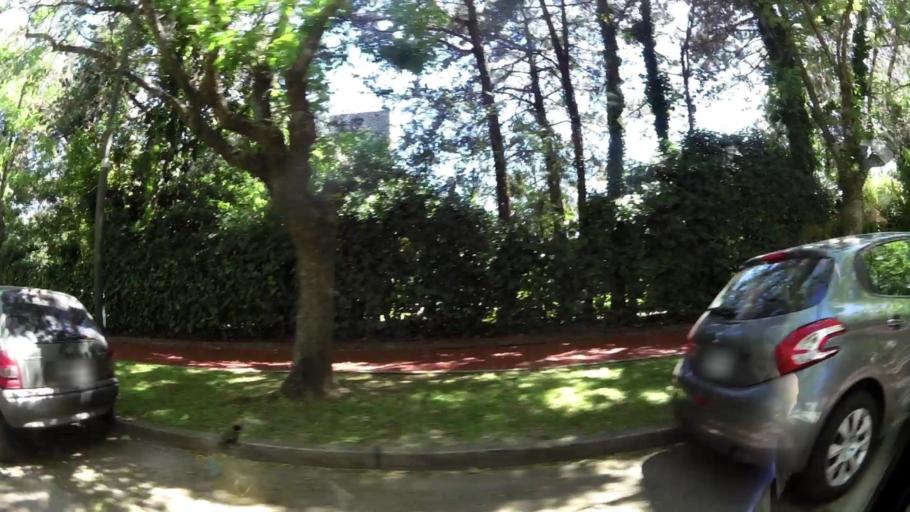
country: AR
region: Buenos Aires
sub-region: Partido de San Isidro
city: San Isidro
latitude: -34.4775
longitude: -58.4892
